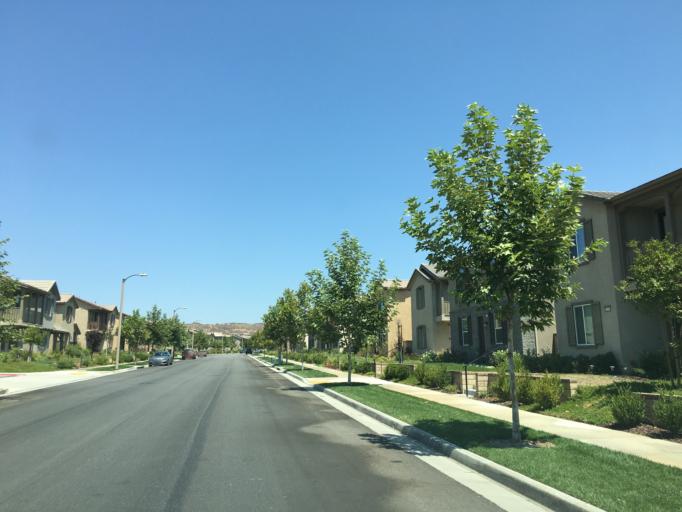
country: US
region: California
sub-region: Los Angeles County
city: Valencia
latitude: 34.4539
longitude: -118.5641
